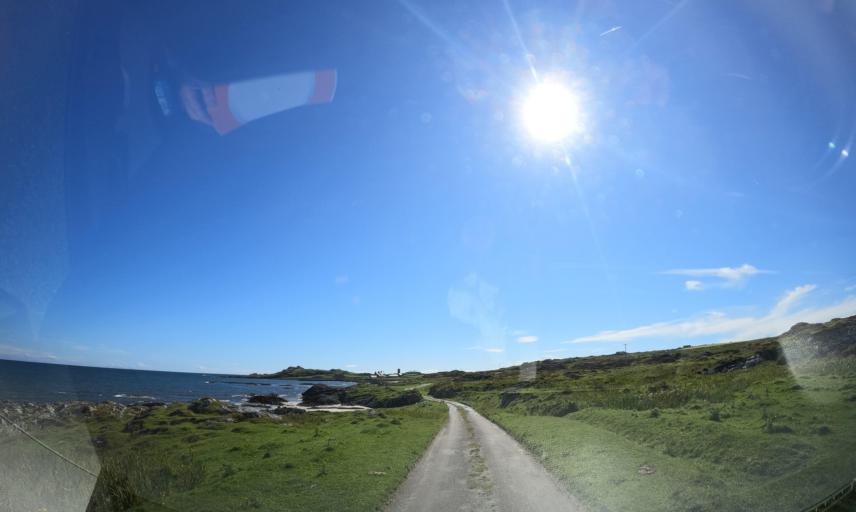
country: GB
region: Scotland
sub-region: Eilean Siar
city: Barra
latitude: 56.4549
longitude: -6.8946
